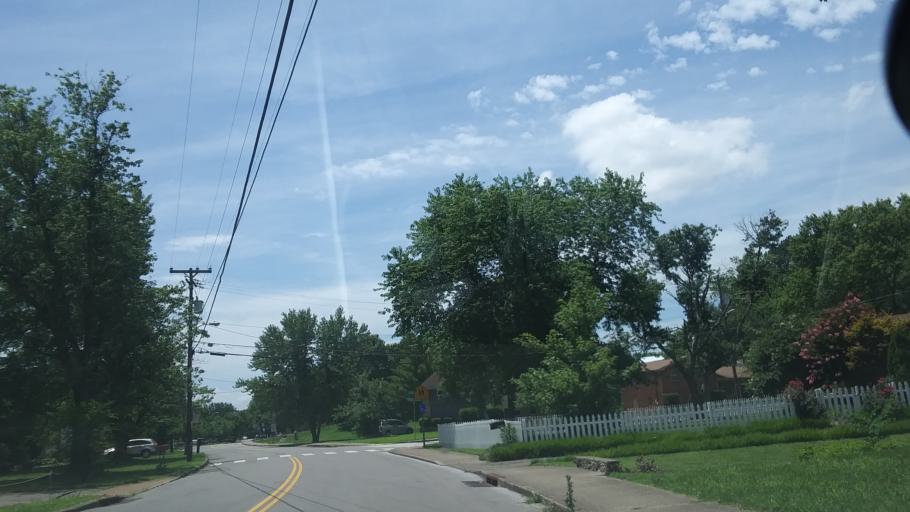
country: US
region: Tennessee
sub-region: Rutherford County
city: La Vergne
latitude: 36.0797
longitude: -86.6279
